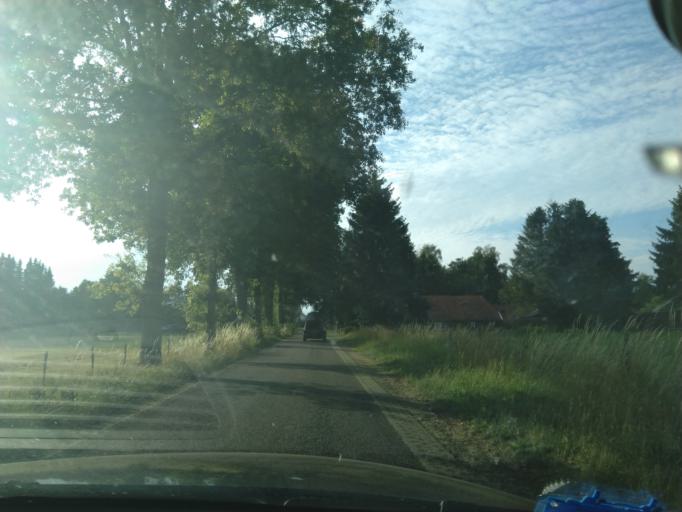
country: NL
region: Groningen
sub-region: Gemeente  Oldambt
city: Winschoten
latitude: 53.0985
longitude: 7.0788
